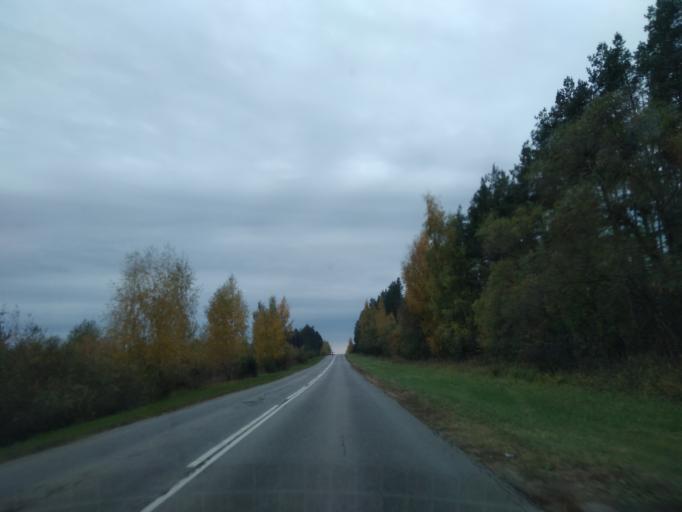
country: RU
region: Lipetsk
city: Zadonsk
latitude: 52.3404
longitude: 38.9204
